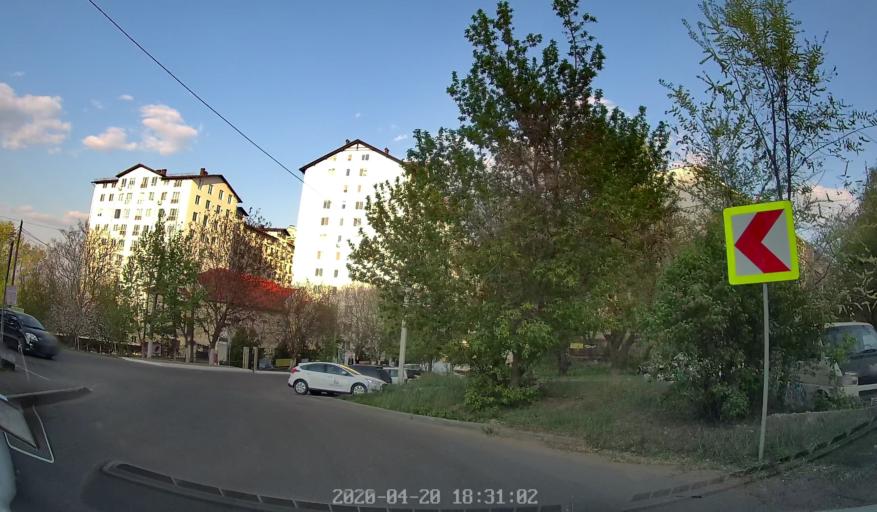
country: MD
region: Chisinau
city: Chisinau
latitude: 46.9870
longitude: 28.8392
